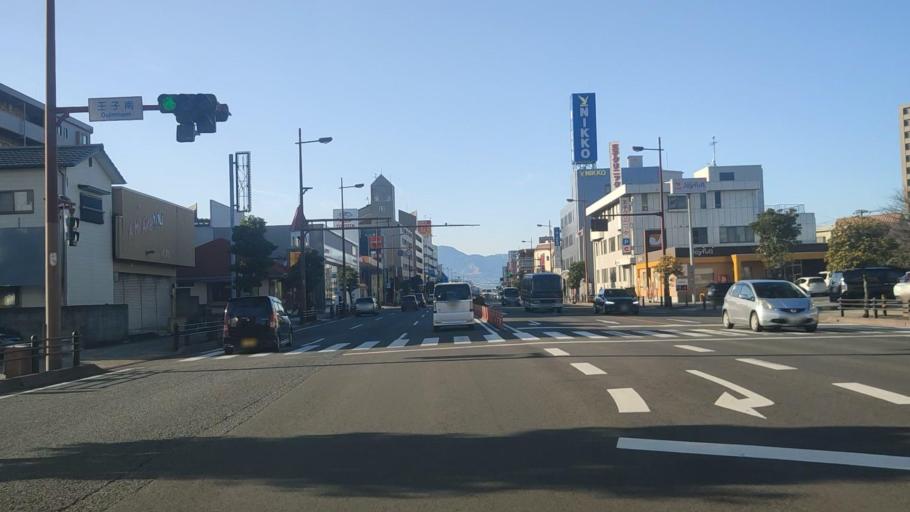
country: JP
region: Oita
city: Oita
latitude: 33.2419
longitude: 131.5917
